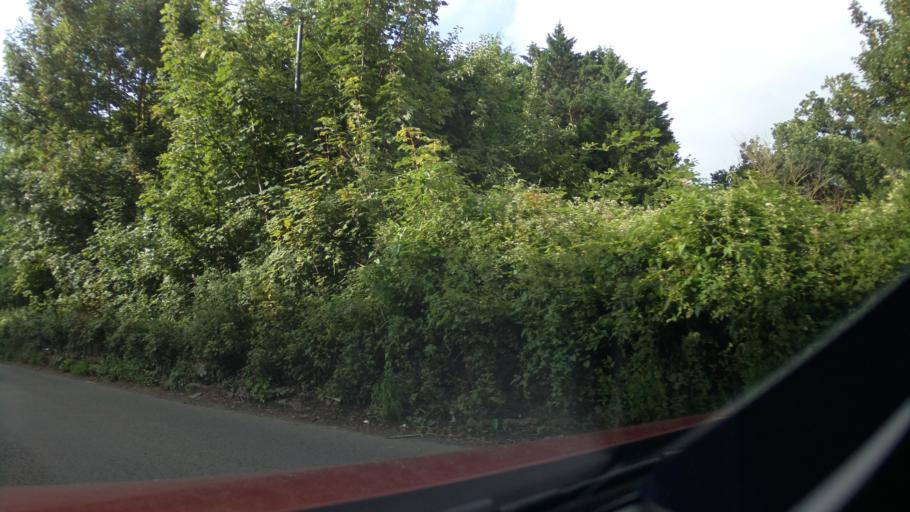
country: GB
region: England
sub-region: North Somerset
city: Nailsea
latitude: 51.4395
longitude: -2.7264
